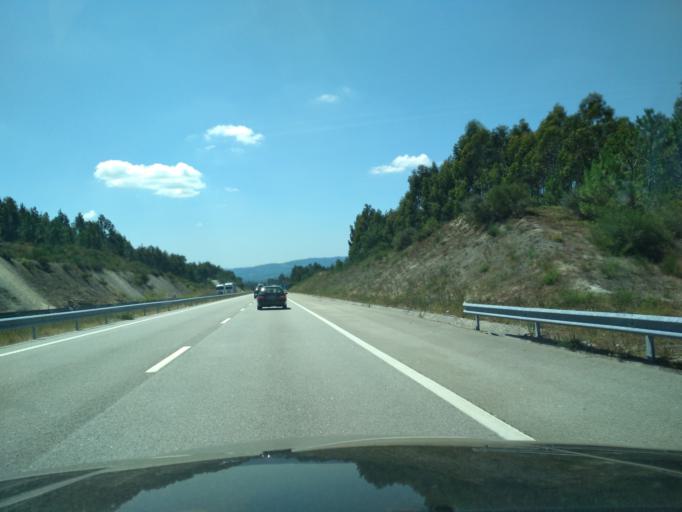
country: PT
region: Braga
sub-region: Fafe
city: Fafe
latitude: 41.4420
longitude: -8.1109
